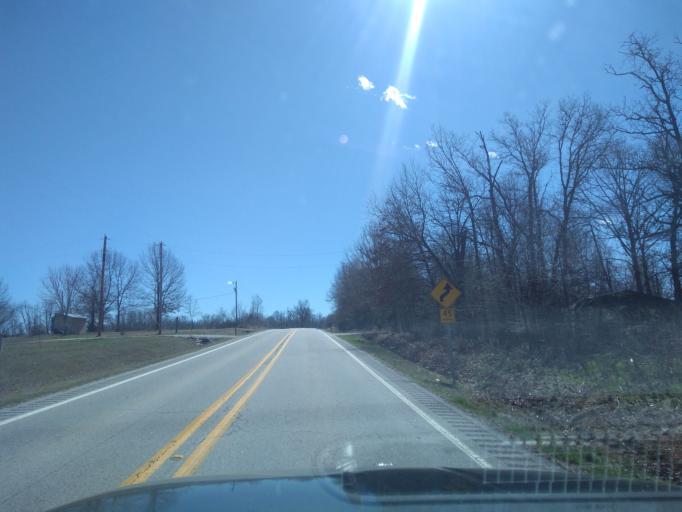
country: US
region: Arkansas
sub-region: Washington County
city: Farmington
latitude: 36.0941
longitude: -94.3319
